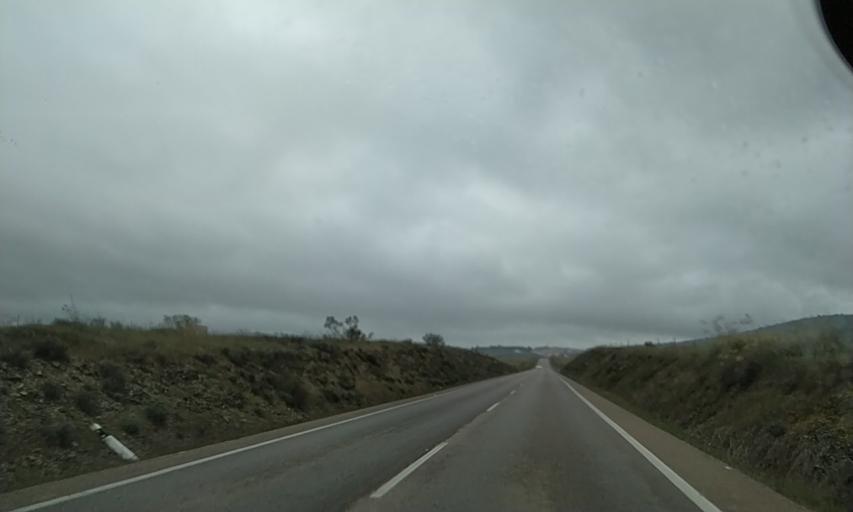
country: ES
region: Extremadura
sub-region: Provincia de Caceres
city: Caceres
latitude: 39.5066
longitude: -6.3917
